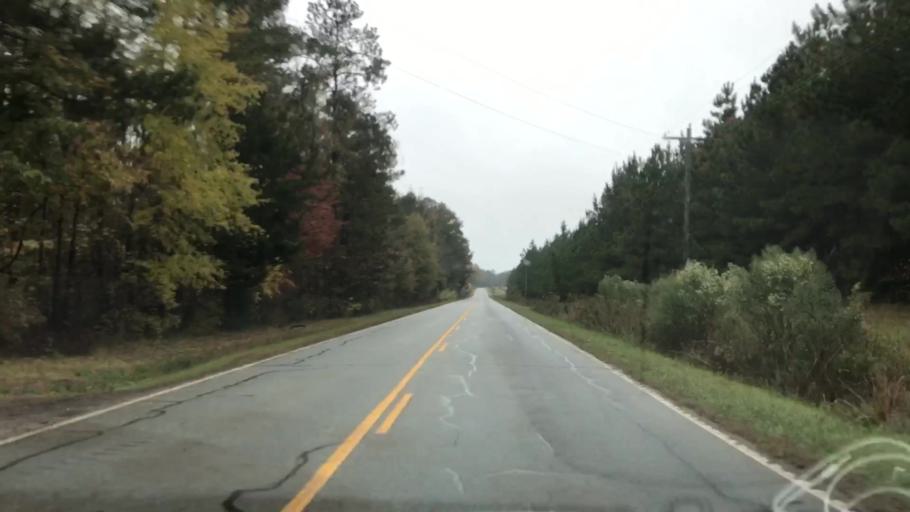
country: US
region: South Carolina
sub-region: Laurens County
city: Joanna
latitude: 34.3622
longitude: -81.7426
